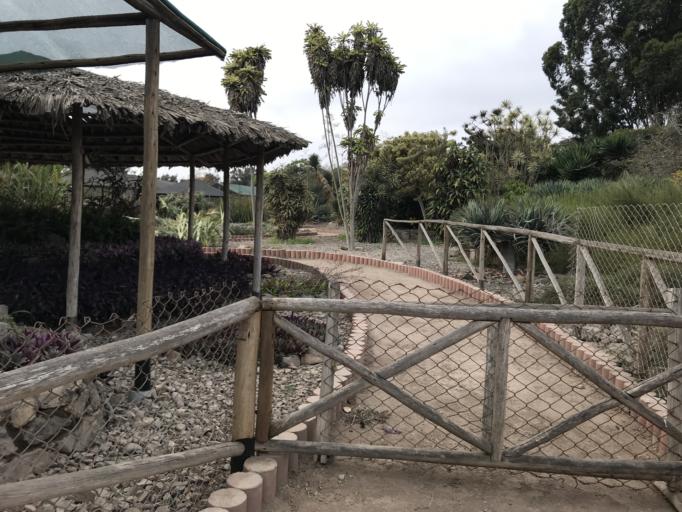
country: PE
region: Callao
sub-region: Callao
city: Callao
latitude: -12.0680
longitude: -77.0876
